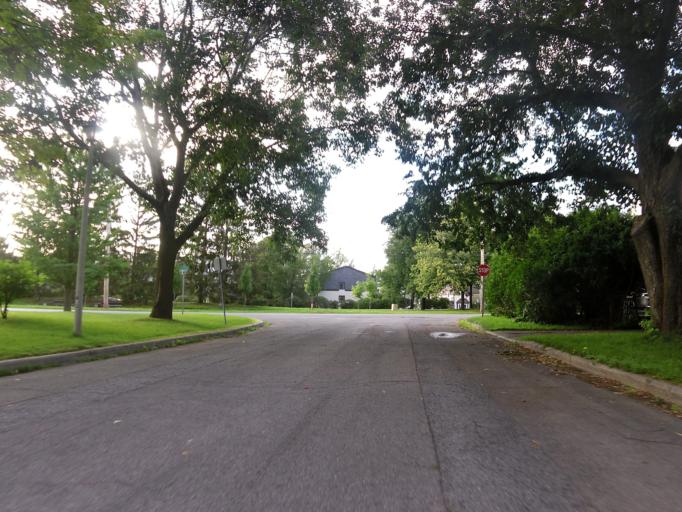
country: CA
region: Ontario
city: Ottawa
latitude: 45.3841
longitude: -75.7661
